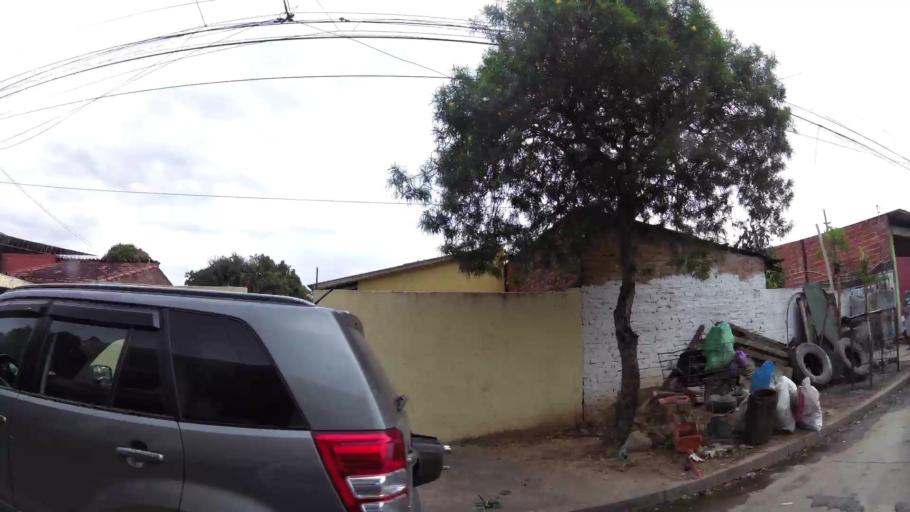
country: BO
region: Santa Cruz
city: Santa Cruz de la Sierra
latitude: -17.7753
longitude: -63.2143
